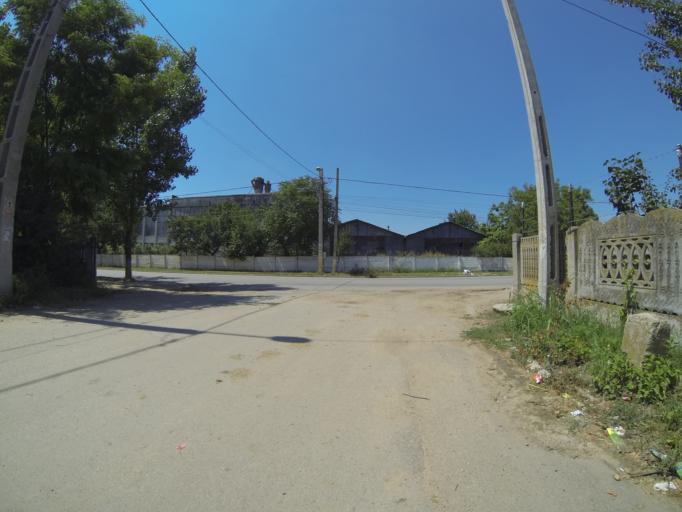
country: RO
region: Dolj
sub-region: Comuna Segarcea
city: Segarcea
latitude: 44.0903
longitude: 23.7331
